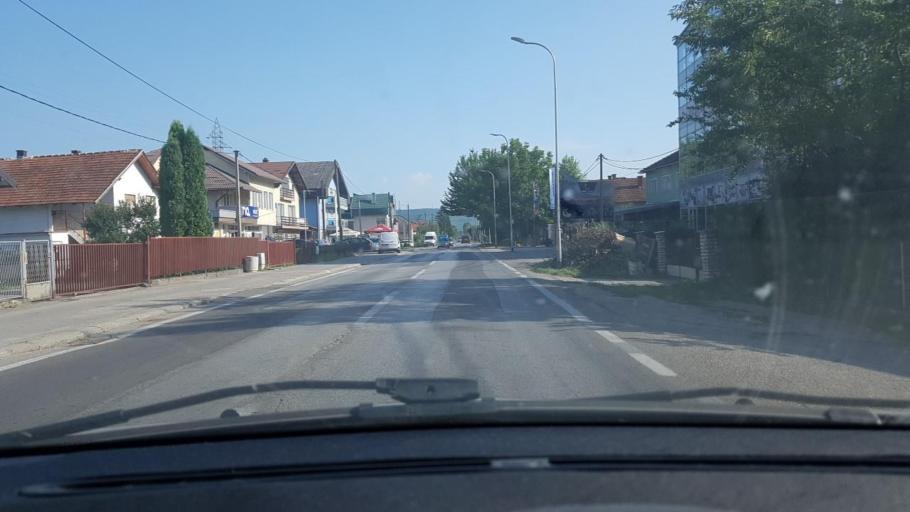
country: BA
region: Federation of Bosnia and Herzegovina
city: Bihac
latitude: 44.8253
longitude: 15.8817
